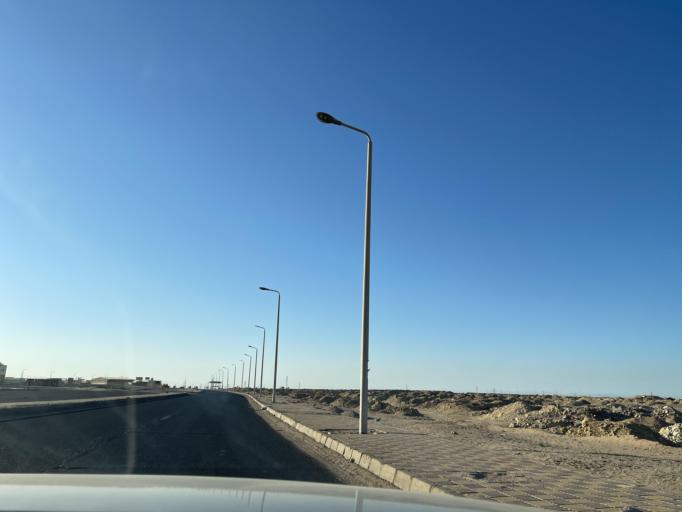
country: EG
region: Red Sea
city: Hurghada
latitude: 27.2222
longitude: 33.7842
